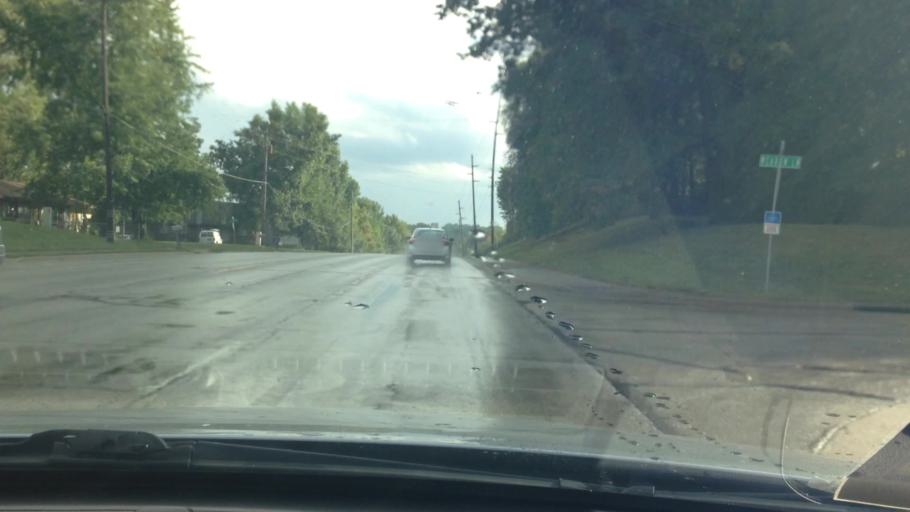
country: US
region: Kansas
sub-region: Leavenworth County
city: Leavenworth
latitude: 39.2855
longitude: -94.9279
